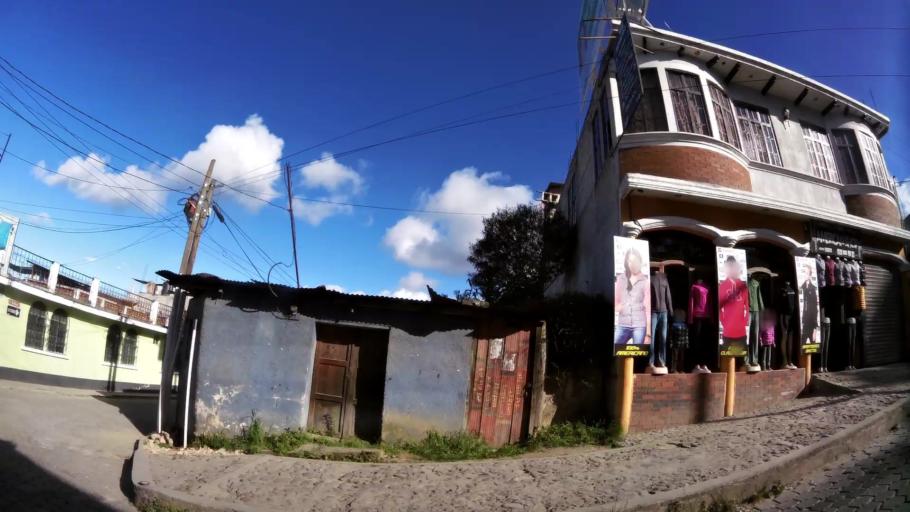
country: GT
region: Quiche
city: Chichicastenango
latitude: 14.9453
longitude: -91.1104
